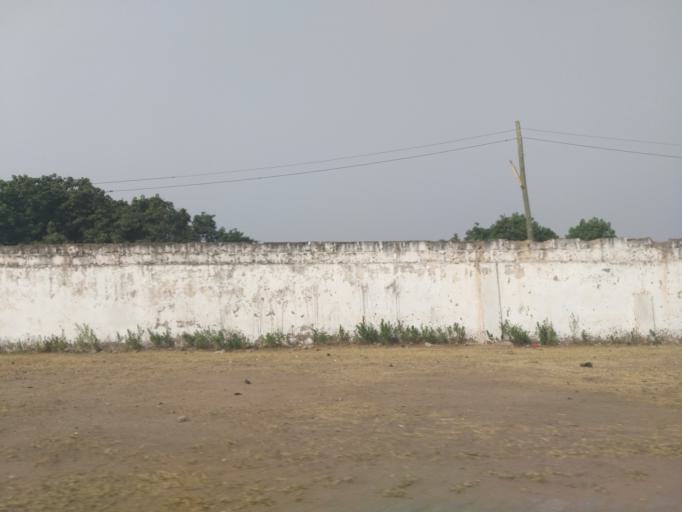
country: GH
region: Greater Accra
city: Accra
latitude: 5.5352
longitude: -0.2164
